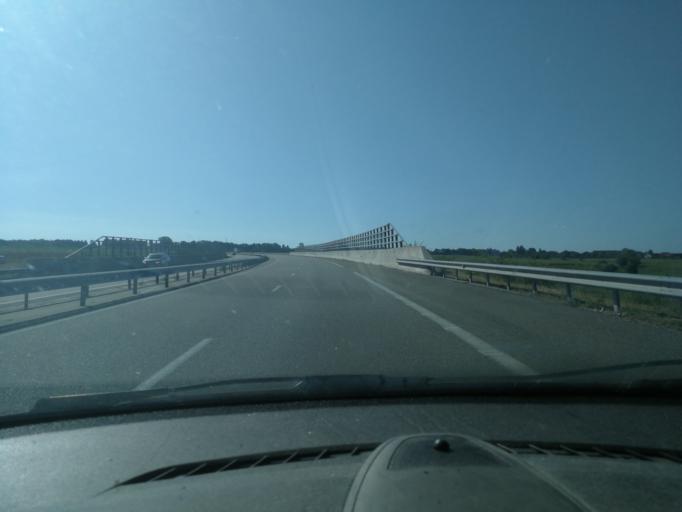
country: FR
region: Lorraine
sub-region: Departement de la Moselle
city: Phalsbourg
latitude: 48.7800
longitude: 7.2285
